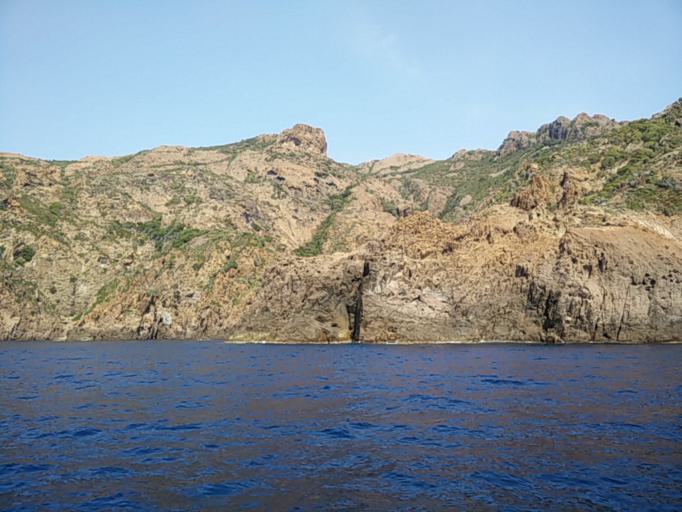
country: FR
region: Corsica
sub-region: Departement de la Corse-du-Sud
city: Cargese
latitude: 42.3516
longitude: 8.5535
